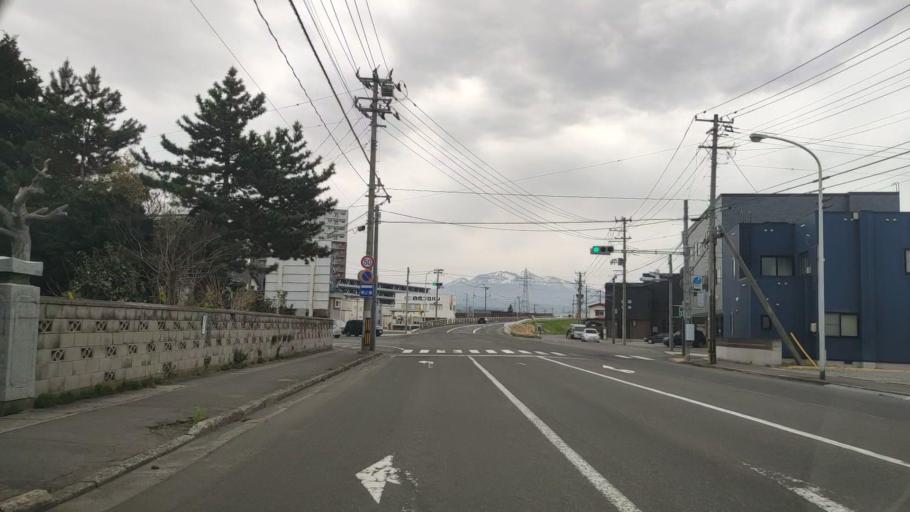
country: JP
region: Aomori
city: Aomori Shi
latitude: 40.8115
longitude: 140.7781
